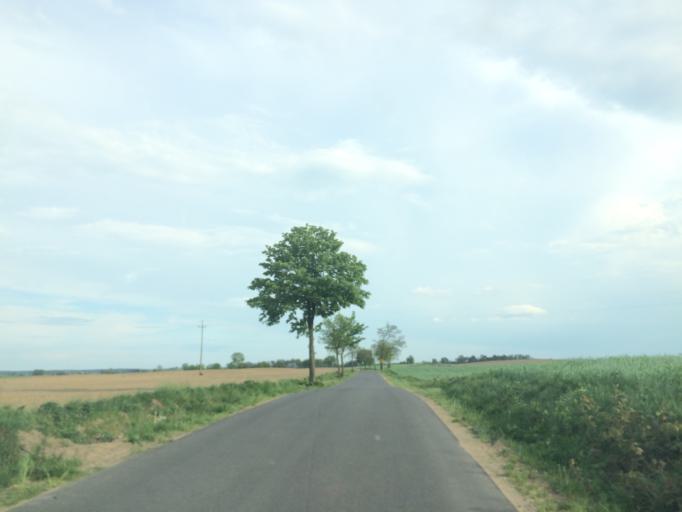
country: PL
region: Kujawsko-Pomorskie
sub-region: Powiat brodnicki
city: Brzozie
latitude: 53.3787
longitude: 19.7086
